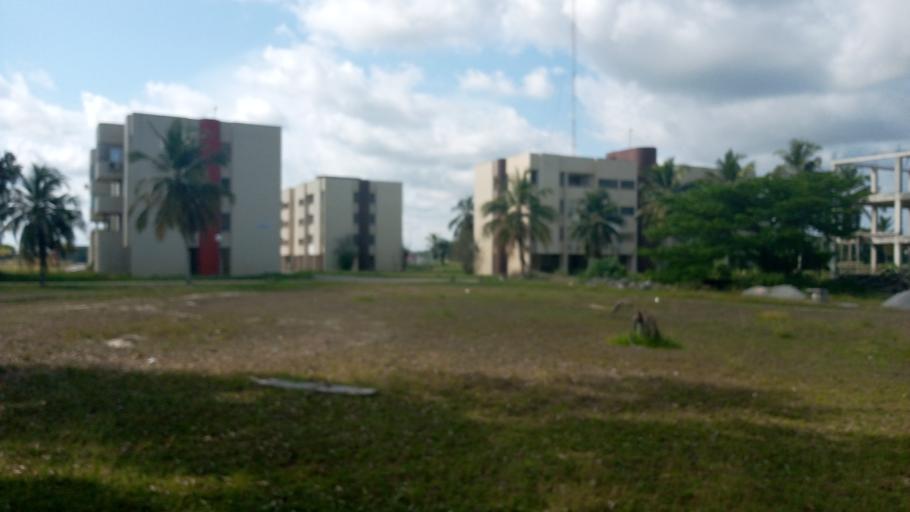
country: CI
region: Sud-Comoe
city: Grand-Bassam
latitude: 5.2300
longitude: -3.7591
